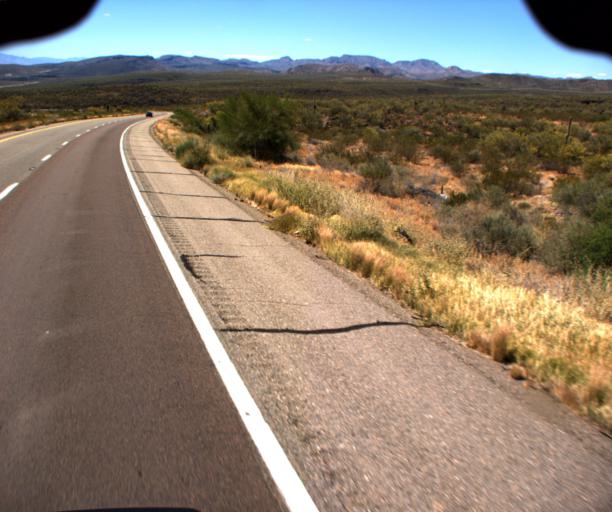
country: US
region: Arizona
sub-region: Yavapai County
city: Bagdad
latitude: 34.4966
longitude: -113.3954
